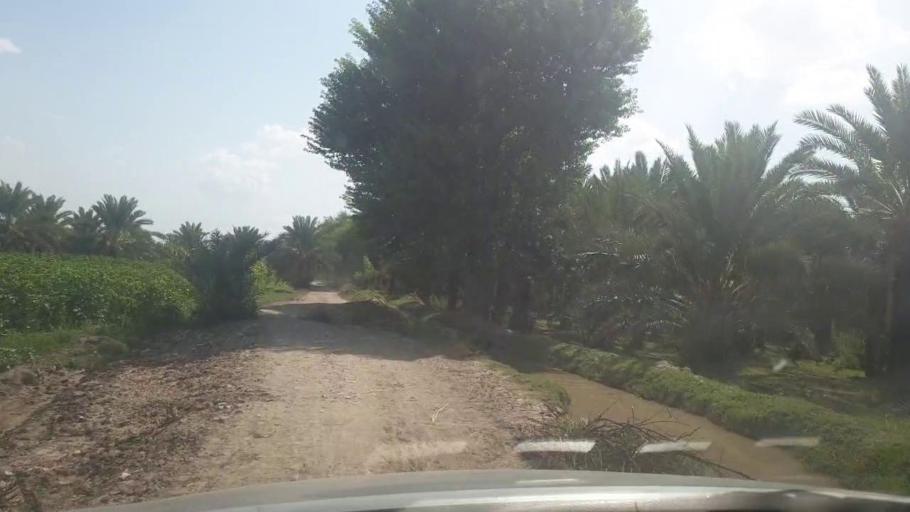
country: PK
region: Sindh
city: Khairpur
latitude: 27.5525
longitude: 68.8089
